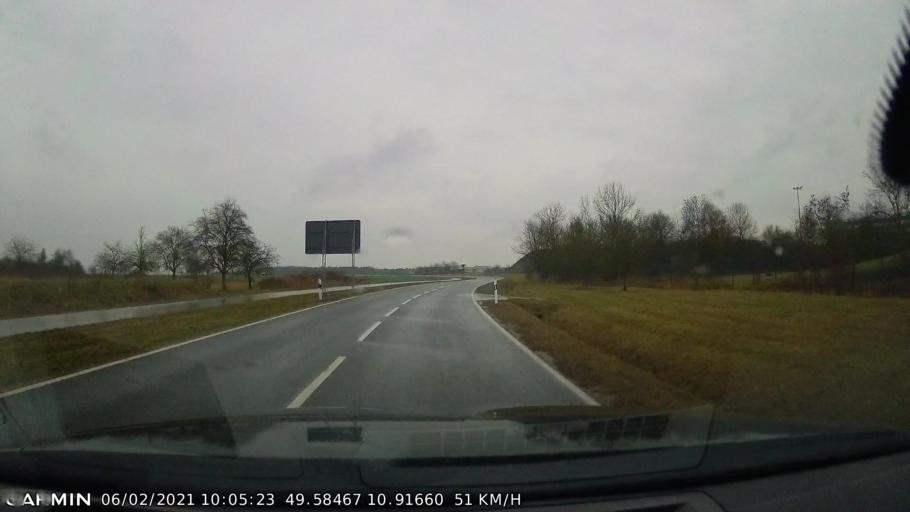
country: DE
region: Bavaria
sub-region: Regierungsbezirk Mittelfranken
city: Herzogenaurach
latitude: 49.5847
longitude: 10.9166
